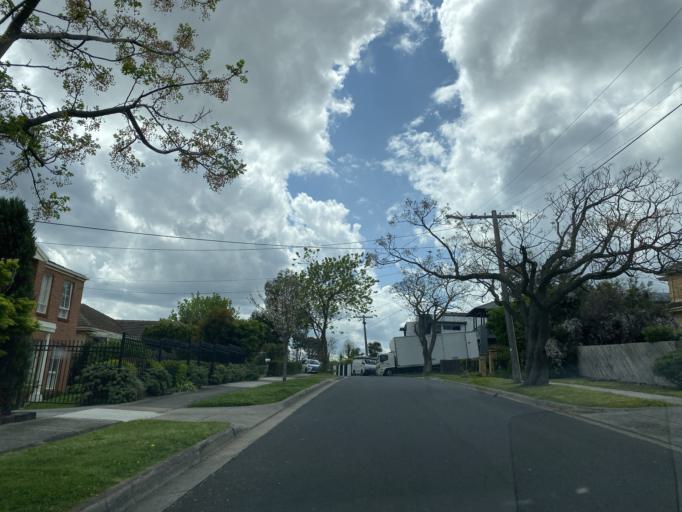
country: AU
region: Victoria
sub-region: Whitehorse
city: Burwood
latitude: -37.8598
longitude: 145.1171
